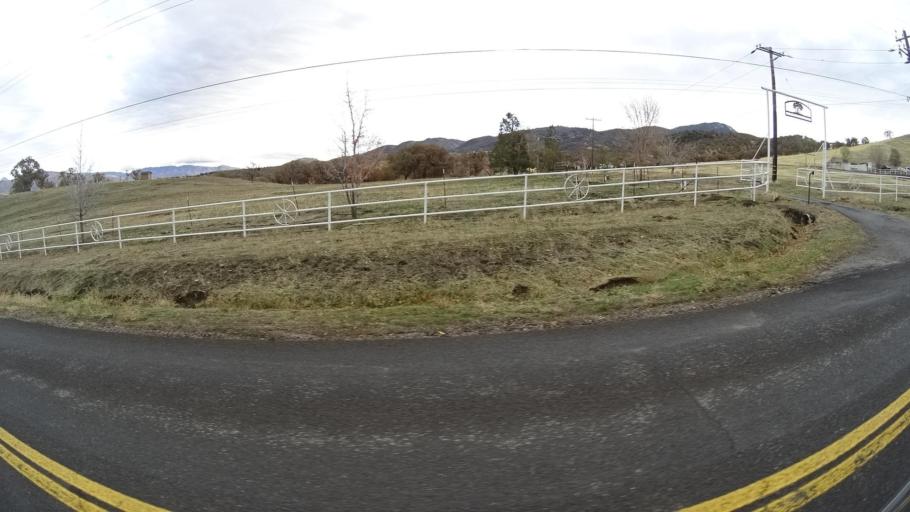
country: US
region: California
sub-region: Kern County
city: Golden Hills
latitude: 35.1077
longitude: -118.5243
